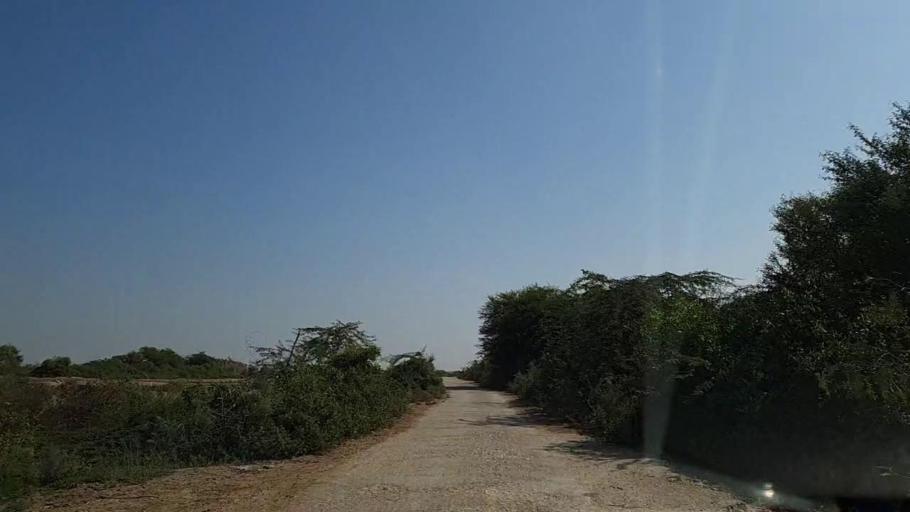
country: PK
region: Sindh
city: Chuhar Jamali
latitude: 24.4616
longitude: 68.1087
